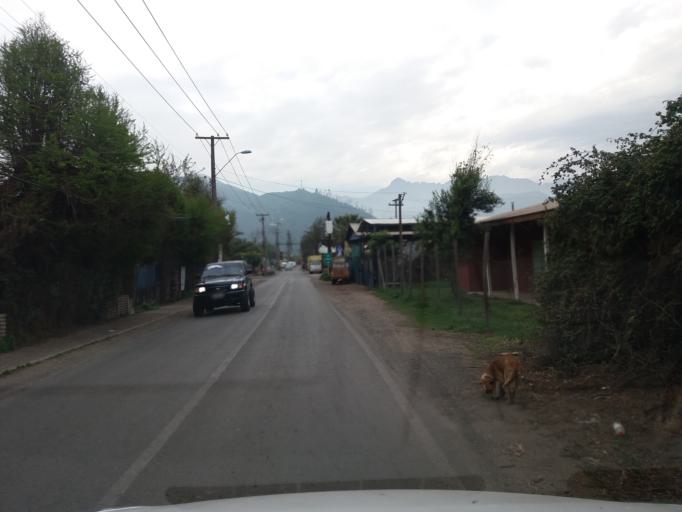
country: CL
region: Valparaiso
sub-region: Provincia de Quillota
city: Hacienda La Calera
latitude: -32.8482
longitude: -71.1037
